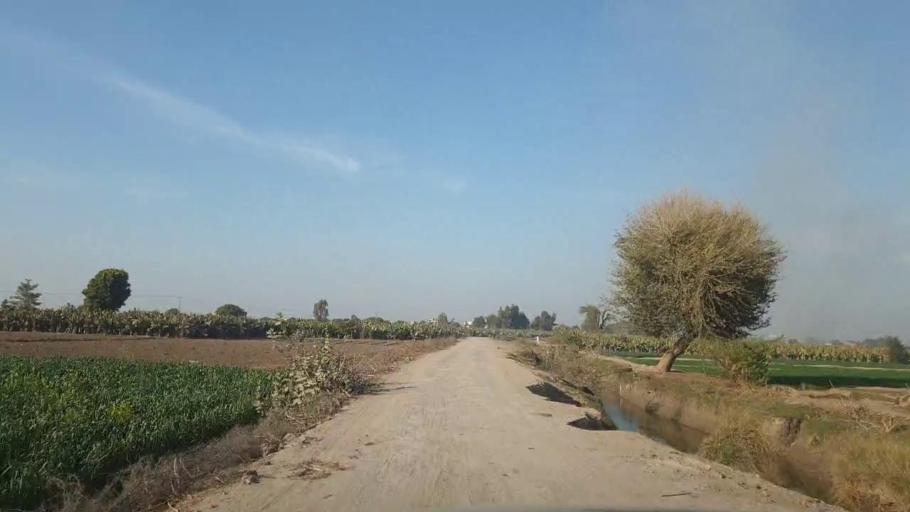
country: PK
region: Sindh
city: Tando Adam
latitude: 25.7051
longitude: 68.7021
